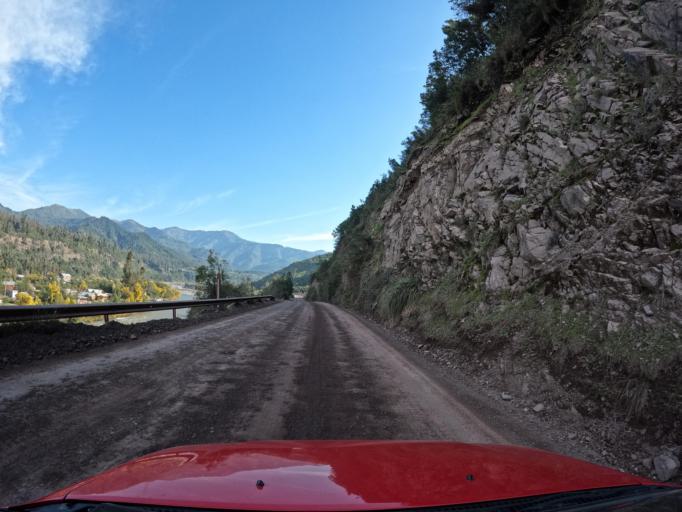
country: CL
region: O'Higgins
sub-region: Provincia de Colchagua
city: Chimbarongo
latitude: -34.9965
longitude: -70.8226
